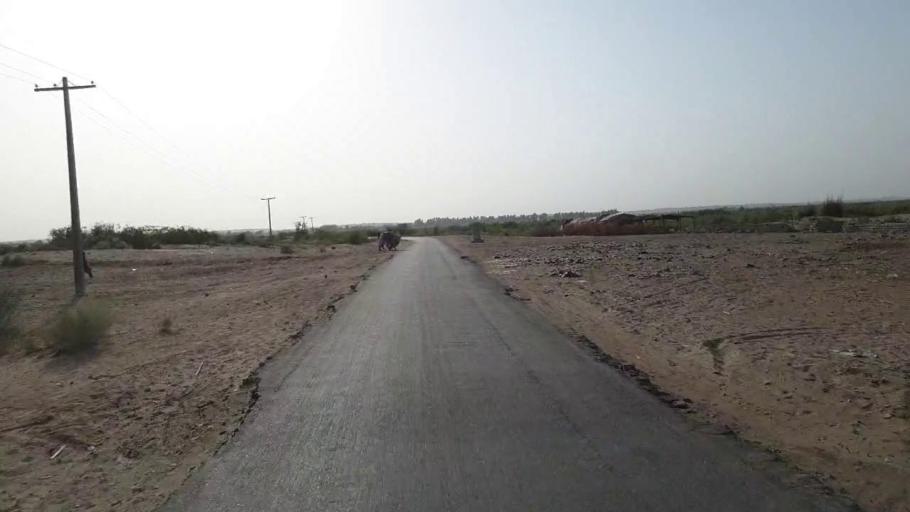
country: PK
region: Sindh
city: Jam Sahib
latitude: 26.4374
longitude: 68.8691
